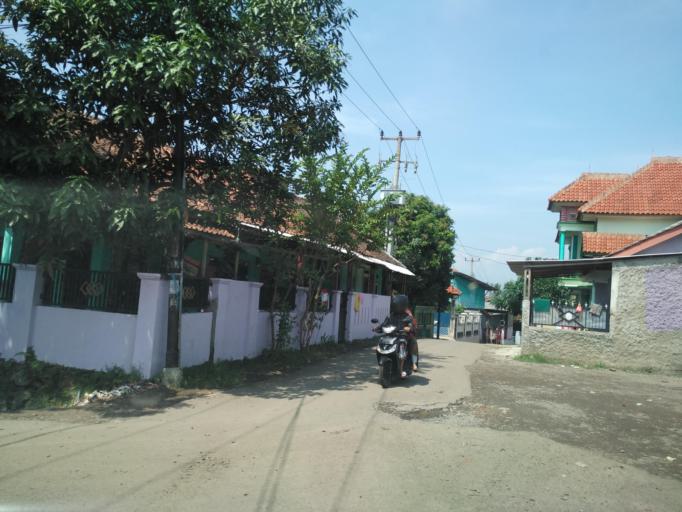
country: ID
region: West Java
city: Ciranjang-hilir
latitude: -6.8221
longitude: 107.1172
